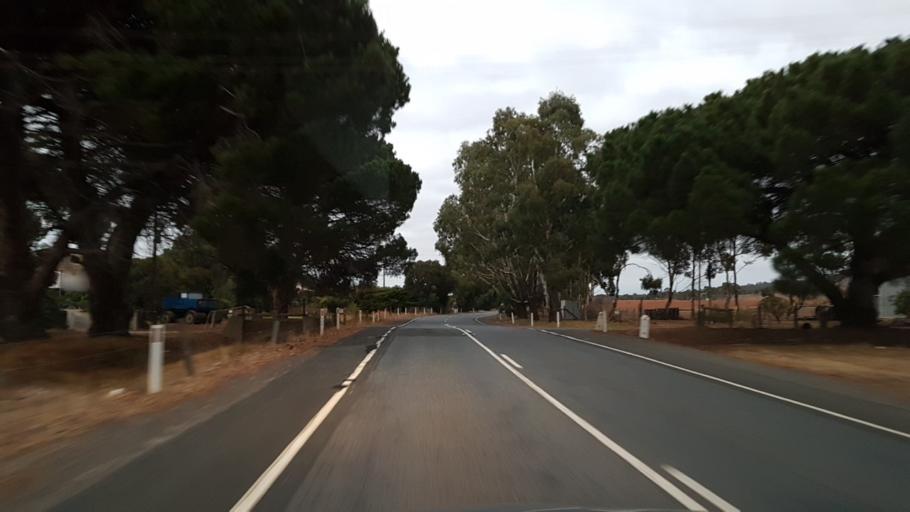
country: AU
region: South Australia
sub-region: Mount Barker
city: Callington
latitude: -35.0585
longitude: 139.0114
